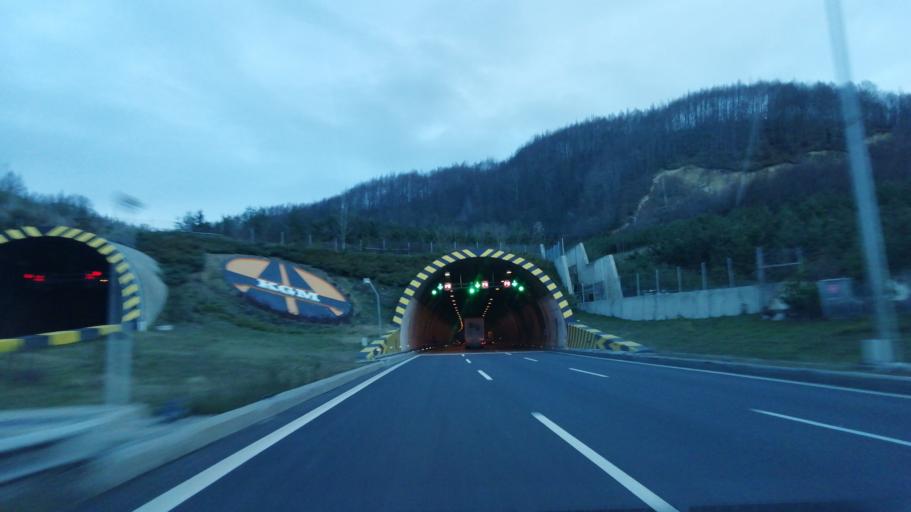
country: TR
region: Duzce
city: Kaynasli
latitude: 40.7357
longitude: 31.4487
